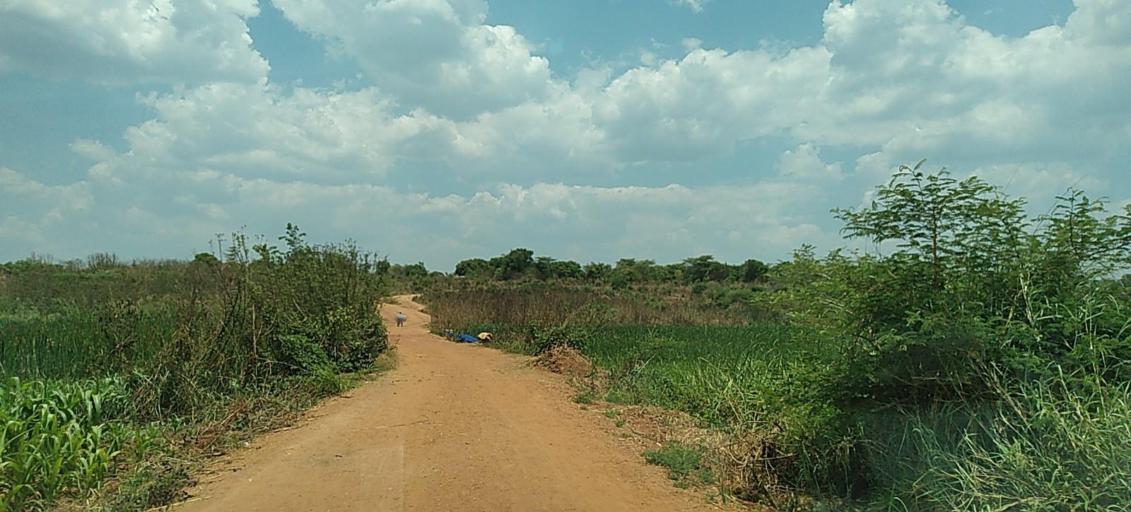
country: ZM
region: Copperbelt
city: Luanshya
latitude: -13.3717
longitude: 28.4180
